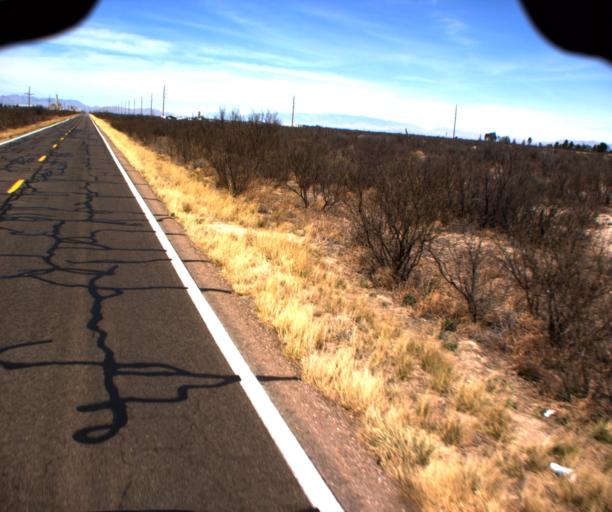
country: US
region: Arizona
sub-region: Cochise County
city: Willcox
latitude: 32.0200
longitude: -109.8709
